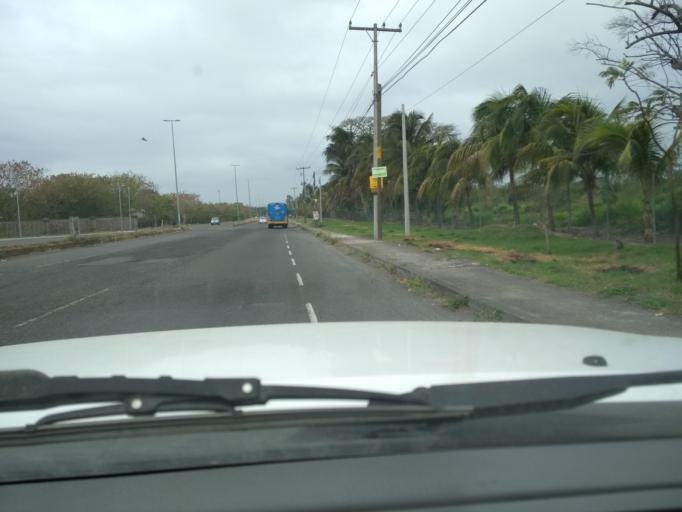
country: MX
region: Veracruz
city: Boca del Rio
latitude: 19.0929
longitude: -96.1123
